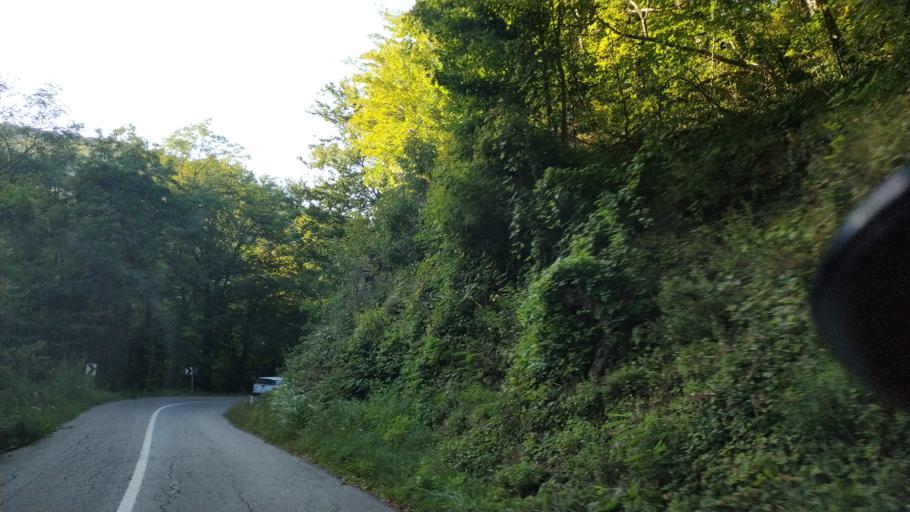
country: RS
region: Central Serbia
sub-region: Rasinski Okrug
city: Krusevac
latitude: 43.4534
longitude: 21.3587
